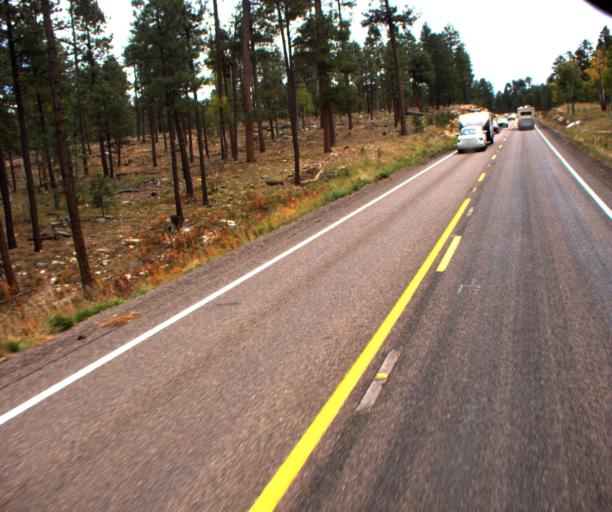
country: US
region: Arizona
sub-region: Navajo County
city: Heber-Overgaard
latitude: 34.2992
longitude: -110.8711
